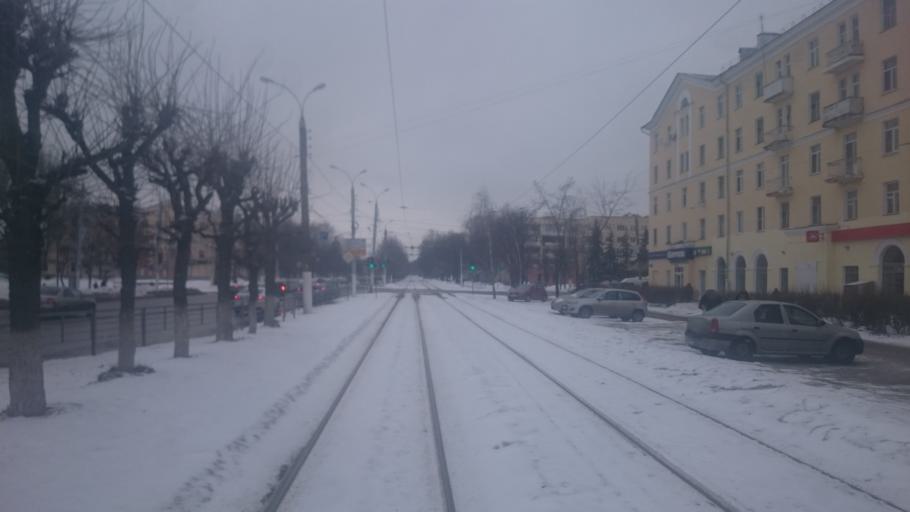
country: RU
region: Tverskaya
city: Tver
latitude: 56.8739
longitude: 35.8525
